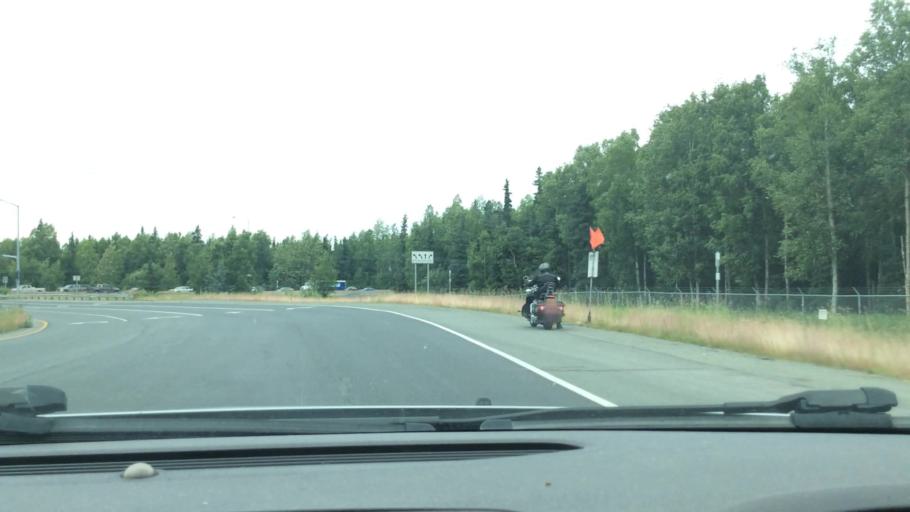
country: US
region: Alaska
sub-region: Anchorage Municipality
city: Anchorage
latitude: 61.2258
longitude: -149.7755
